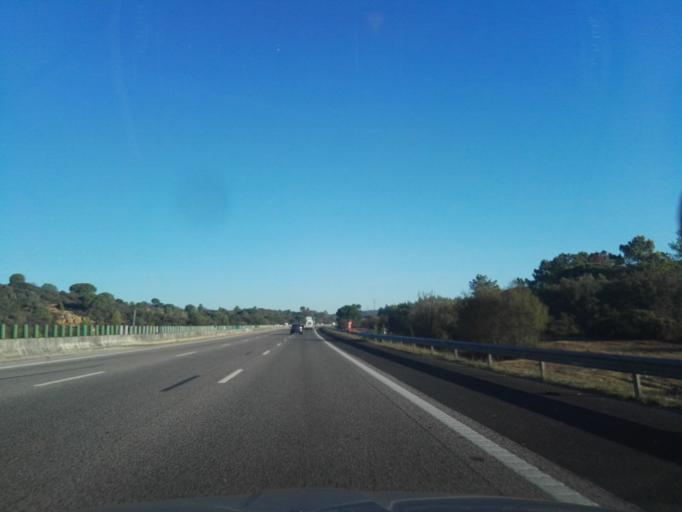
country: PT
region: Lisbon
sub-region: Azambuja
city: Azambuja
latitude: 39.0764
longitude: -8.9327
